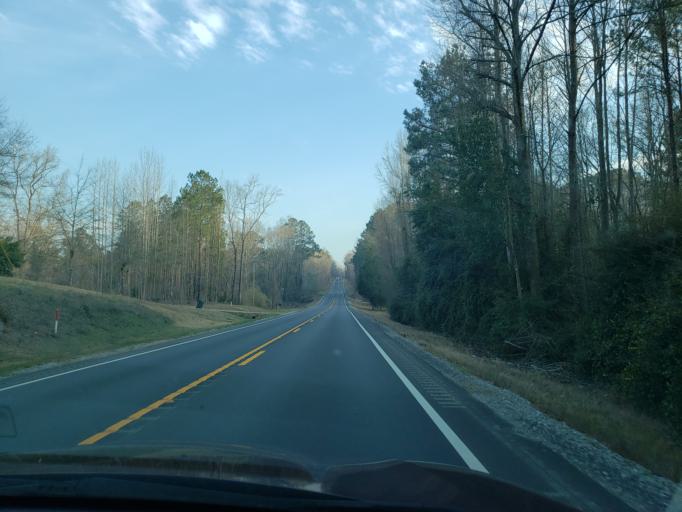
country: US
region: Alabama
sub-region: Hale County
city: Greensboro
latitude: 32.8173
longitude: -87.5986
